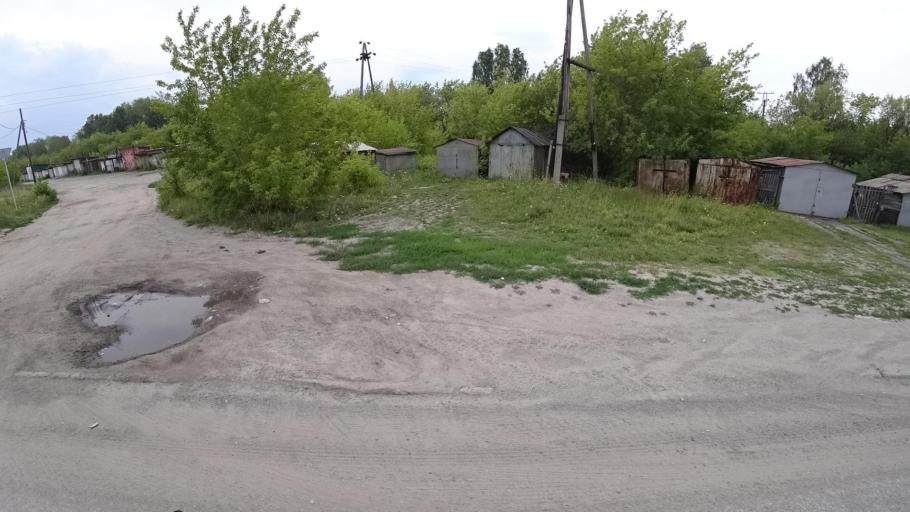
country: RU
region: Sverdlovsk
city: Kamyshlov
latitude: 56.8453
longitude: 62.7454
